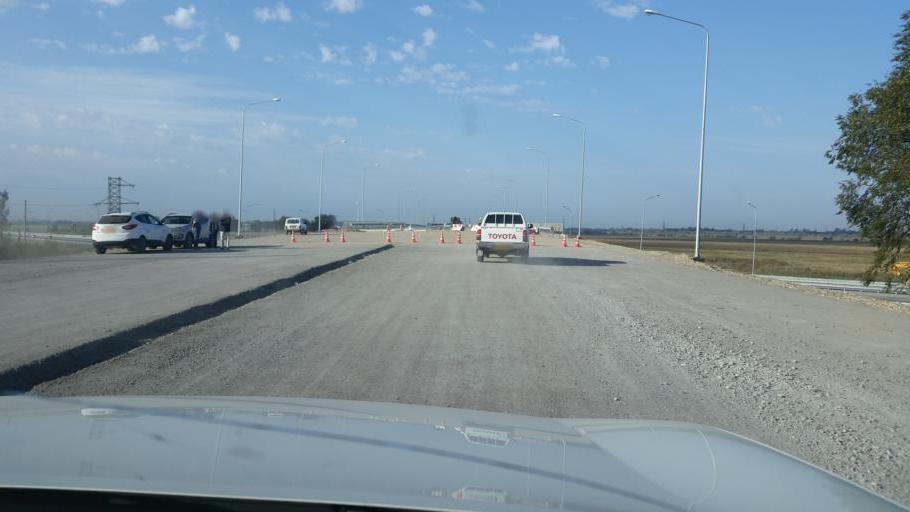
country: KZ
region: Almaty Oblysy
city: Energeticheskiy
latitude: 43.4411
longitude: 76.9900
